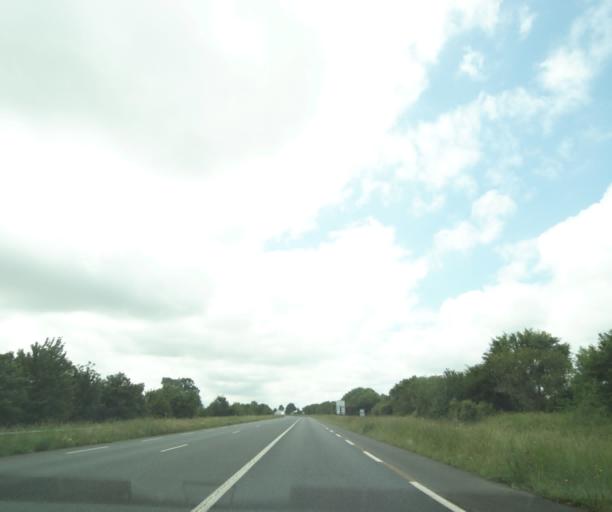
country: FR
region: Poitou-Charentes
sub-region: Departement des Deux-Sevres
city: Airvault
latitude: 46.7796
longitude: -0.2182
